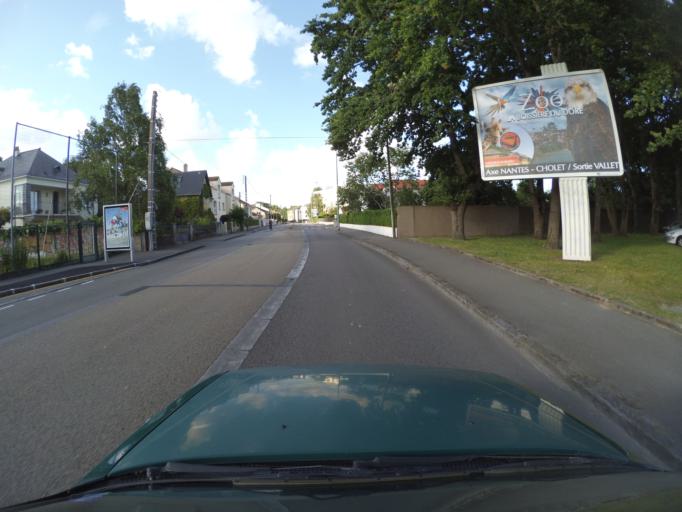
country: FR
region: Pays de la Loire
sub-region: Departement de la Loire-Atlantique
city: Saint-Sebastien-sur-Loire
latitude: 47.1883
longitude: -1.5197
